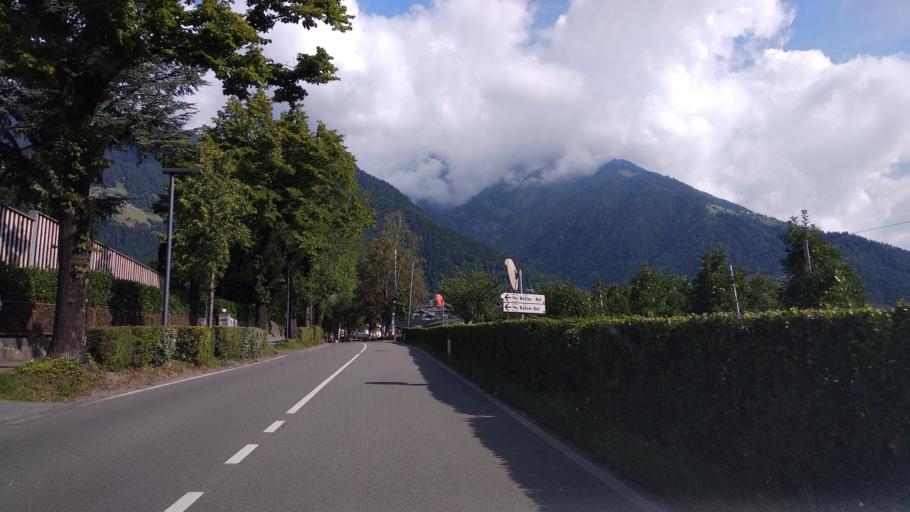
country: IT
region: Trentino-Alto Adige
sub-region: Bolzano
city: Tirolo
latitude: 46.6837
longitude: 11.1607
